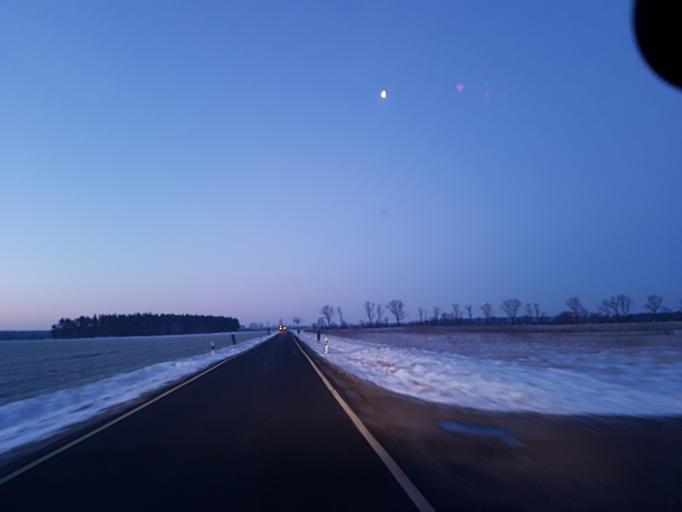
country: DE
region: Brandenburg
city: Muhlberg
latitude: 51.4982
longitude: 13.2805
